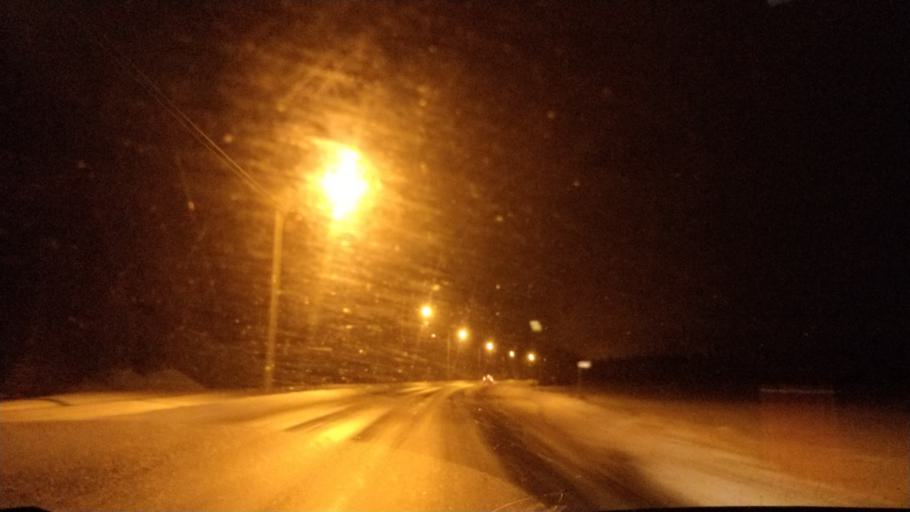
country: FI
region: Lapland
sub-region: Rovaniemi
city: Rovaniemi
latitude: 66.2606
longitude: 25.3422
